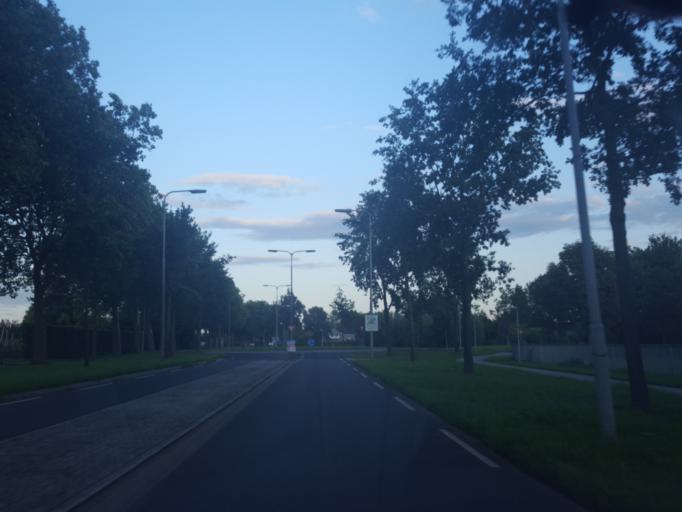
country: NL
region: Gelderland
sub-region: Gemeente Beuningen
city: Beuningen
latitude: 51.8702
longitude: 5.7548
